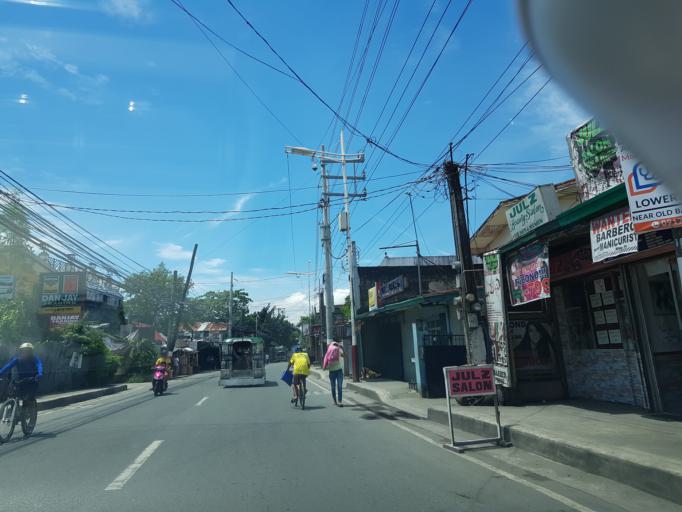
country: PH
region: Calabarzon
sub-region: Province of Rizal
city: Taguig
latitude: 14.4952
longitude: 121.0620
